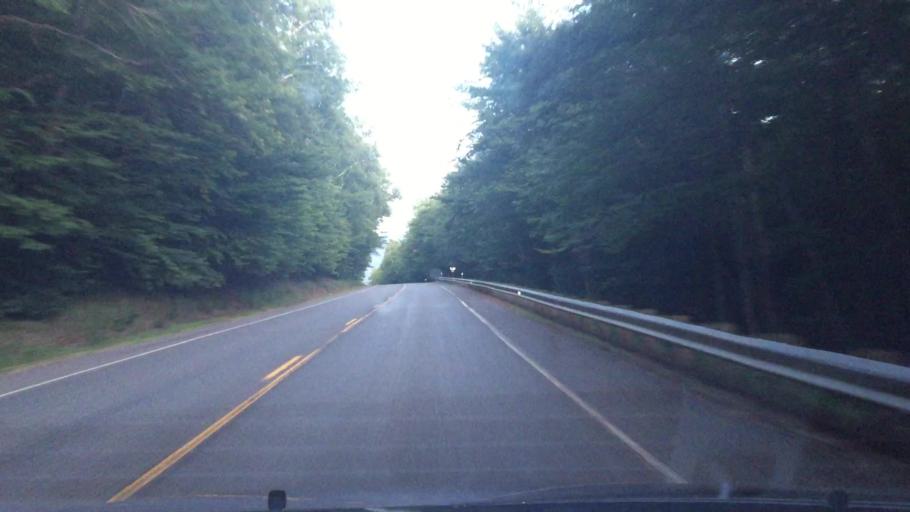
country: US
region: New Hampshire
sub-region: Grafton County
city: Woodstock
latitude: 44.0484
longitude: -71.5625
